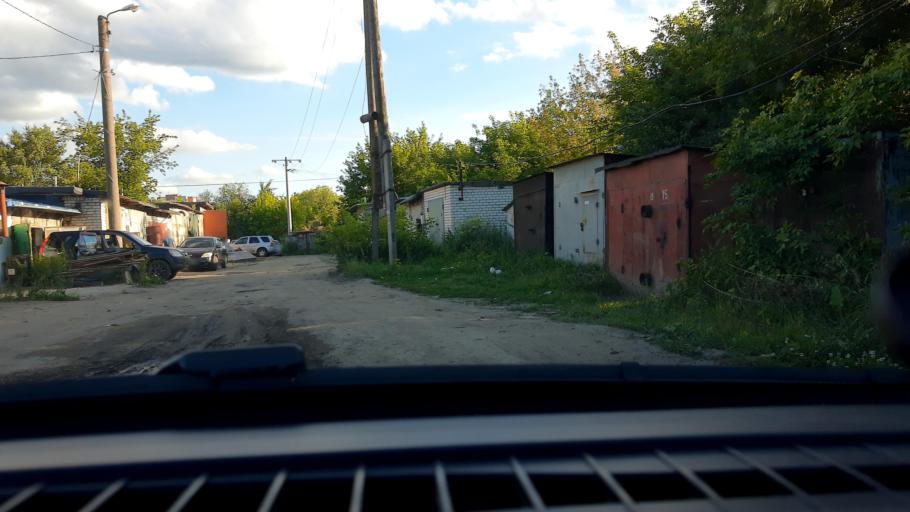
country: RU
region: Nizjnij Novgorod
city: Gorbatovka
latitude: 56.2495
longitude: 43.8241
